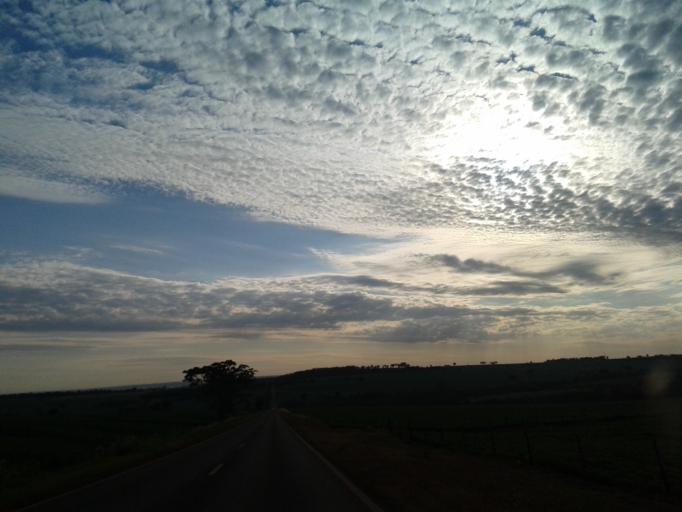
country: BR
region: Minas Gerais
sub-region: Capinopolis
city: Capinopolis
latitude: -18.6903
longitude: -49.4440
